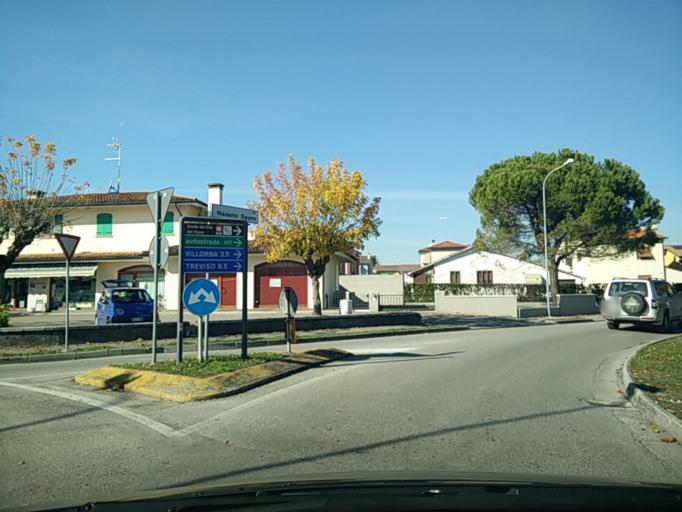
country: IT
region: Veneto
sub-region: Provincia di Treviso
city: Varago
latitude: 45.7209
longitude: 12.2940
